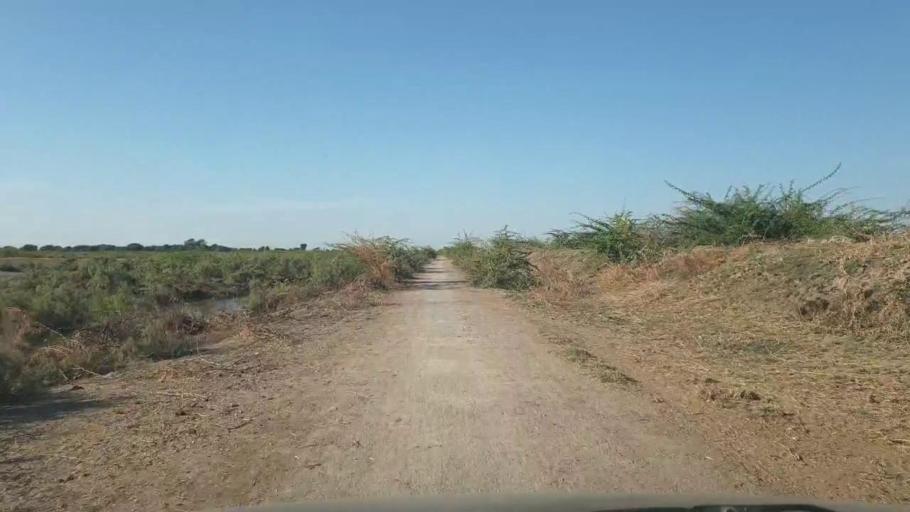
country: PK
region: Sindh
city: Dhoro Naro
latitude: 25.4321
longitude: 69.5525
